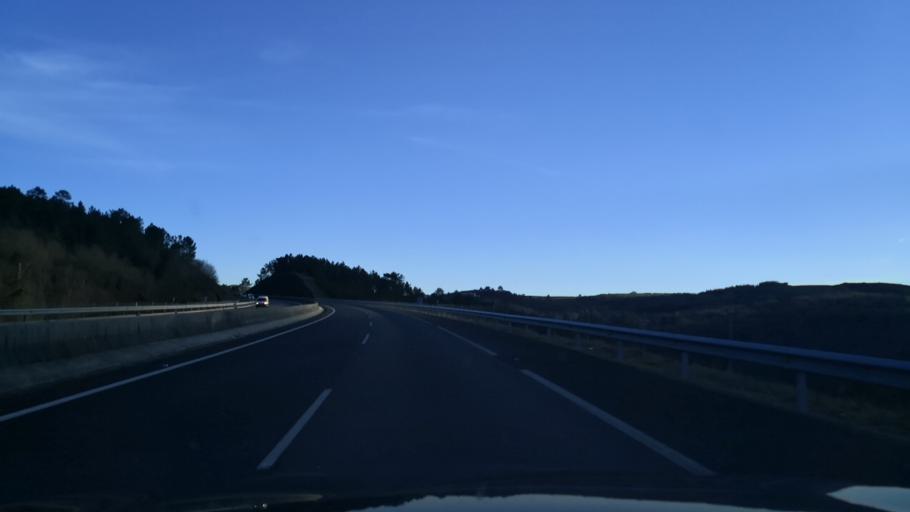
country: ES
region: Galicia
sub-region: Provincia de Pontevedra
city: Lalin
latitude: 42.6066
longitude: -8.1006
